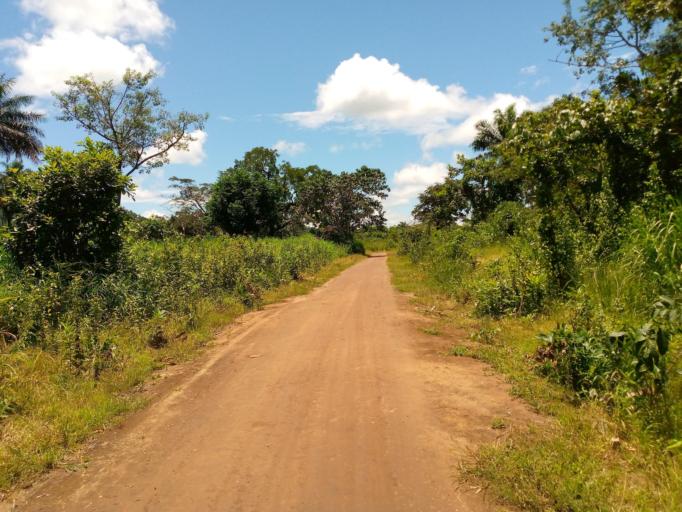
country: SL
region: Northern Province
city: Binkolo
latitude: 9.0842
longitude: -12.1423
